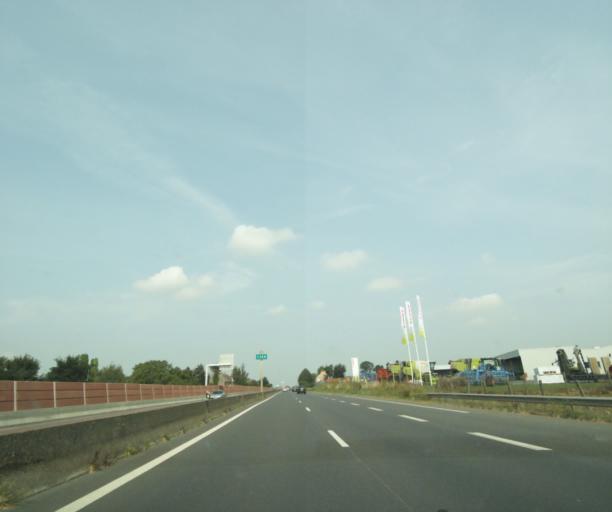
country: FR
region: Lower Normandy
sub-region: Departement du Calvados
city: Bourguebus
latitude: 49.0898
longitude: -0.3067
